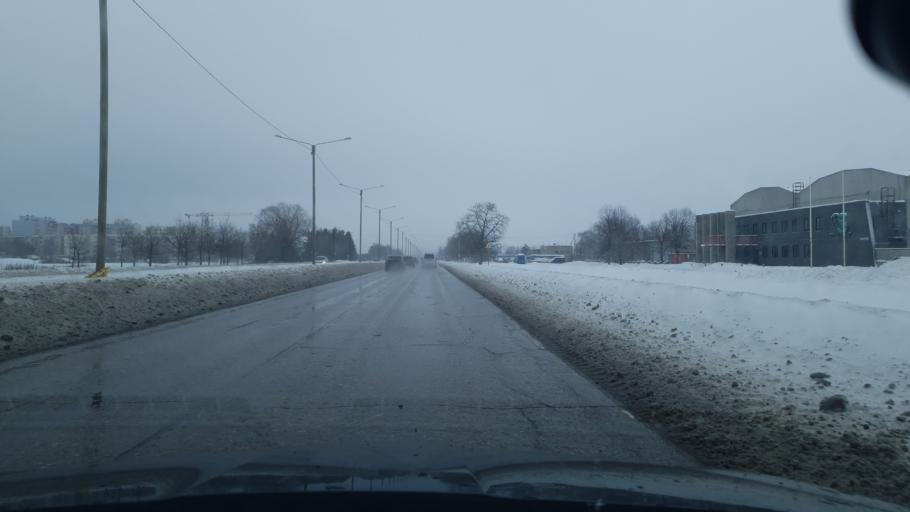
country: EE
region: Harju
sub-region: Tallinna linn
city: Kose
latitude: 59.4382
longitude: 24.8839
